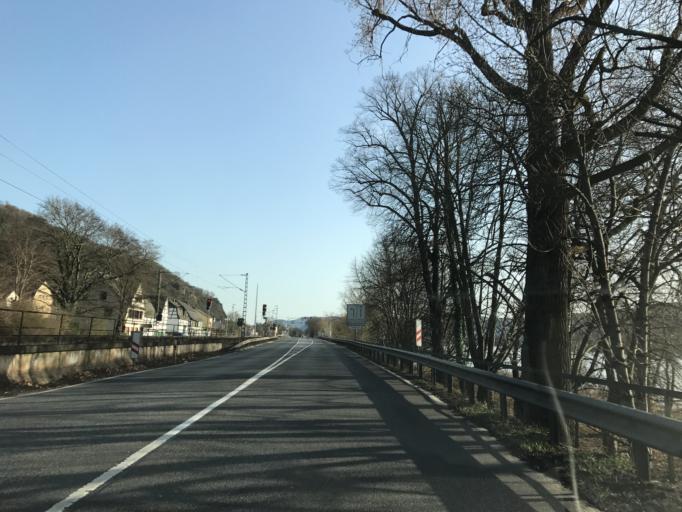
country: DE
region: Rheinland-Pfalz
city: Leubsdorf
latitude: 50.5313
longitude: 7.2939
